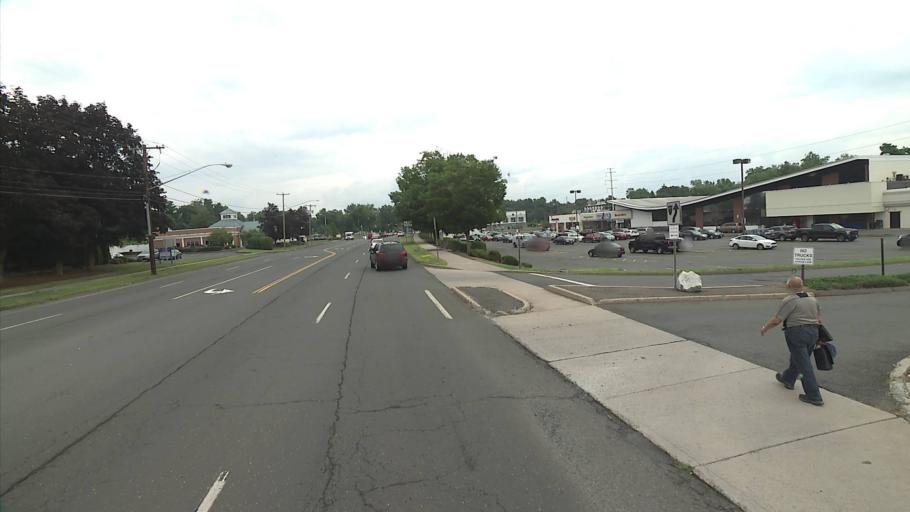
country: US
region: Connecticut
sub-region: Hartford County
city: Wethersfield
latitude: 41.7220
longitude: -72.6678
